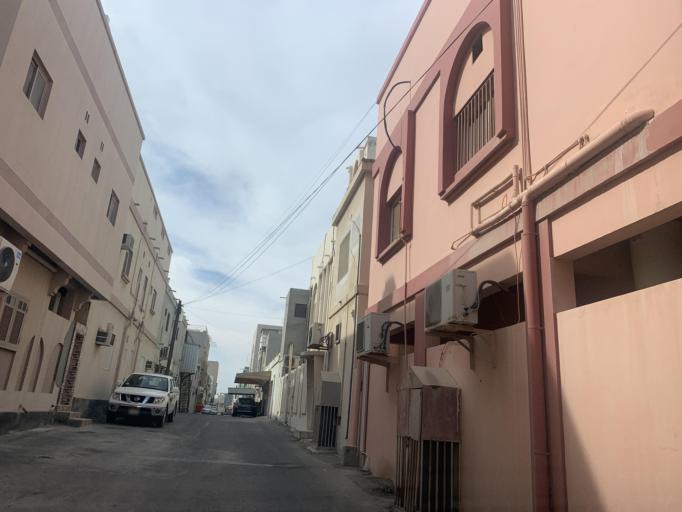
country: BH
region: Central Governorate
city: Madinat Hamad
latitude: 26.1195
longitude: 50.4813
